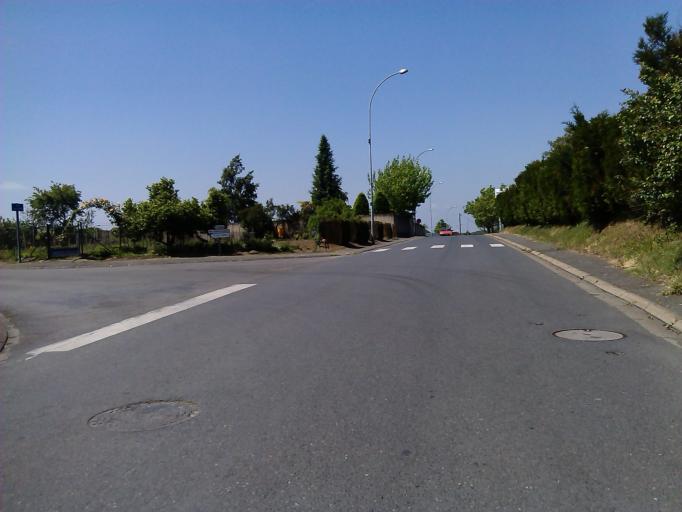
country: FR
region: Centre
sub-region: Departement de l'Indre
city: Saint-Marcel
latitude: 46.6041
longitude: 1.5093
